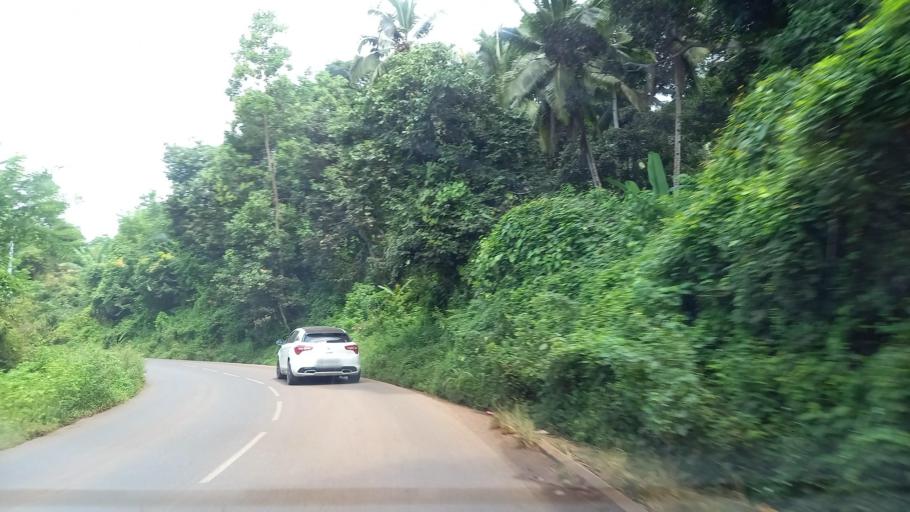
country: YT
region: Mamoudzou
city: Mamoudzou
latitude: -12.7850
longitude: 45.1718
